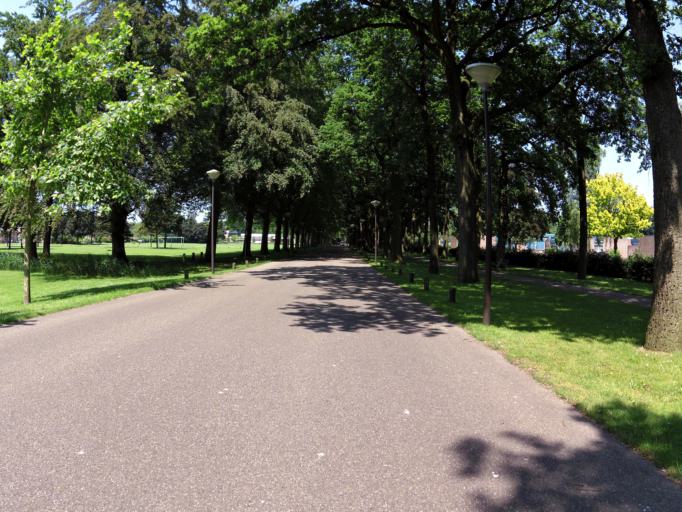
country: NL
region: North Brabant
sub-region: Gemeente Vught
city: Vught
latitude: 51.6433
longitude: 5.3030
